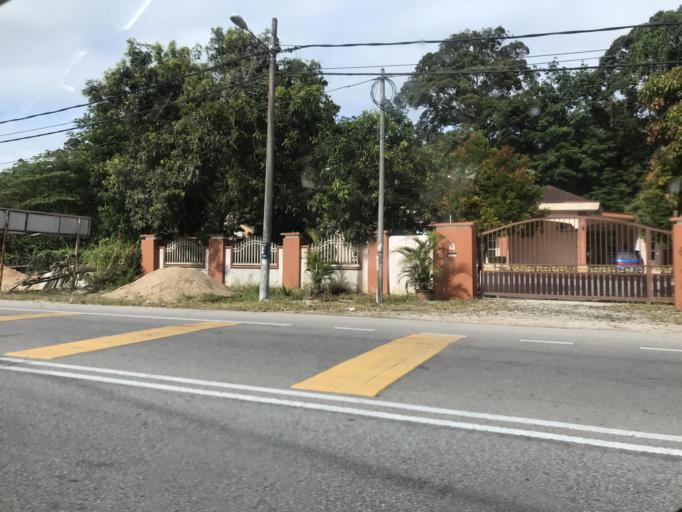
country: MY
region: Kelantan
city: Kota Bharu
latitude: 6.1307
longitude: 102.1778
